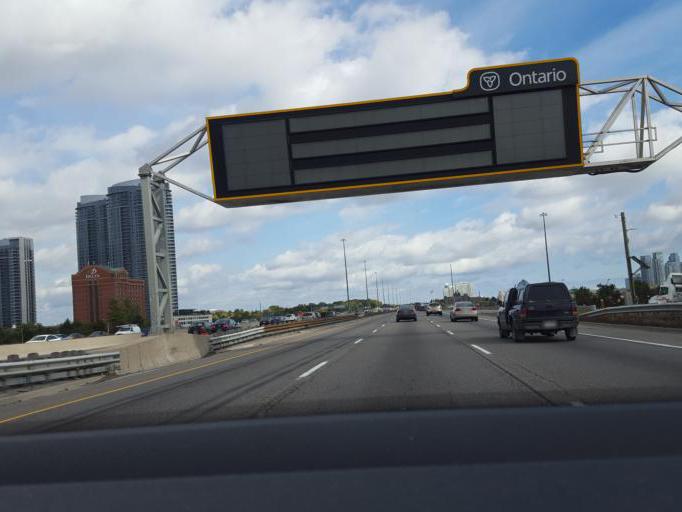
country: CA
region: Ontario
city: Scarborough
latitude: 43.7743
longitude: -79.2864
